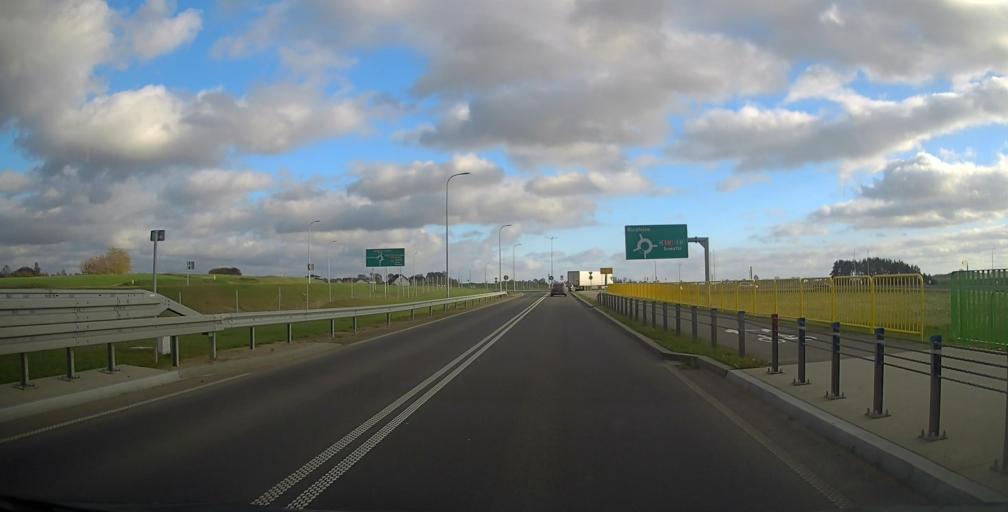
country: PL
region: Podlasie
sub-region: Powiat lomzynski
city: Piatnica
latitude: 53.2496
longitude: 22.1061
